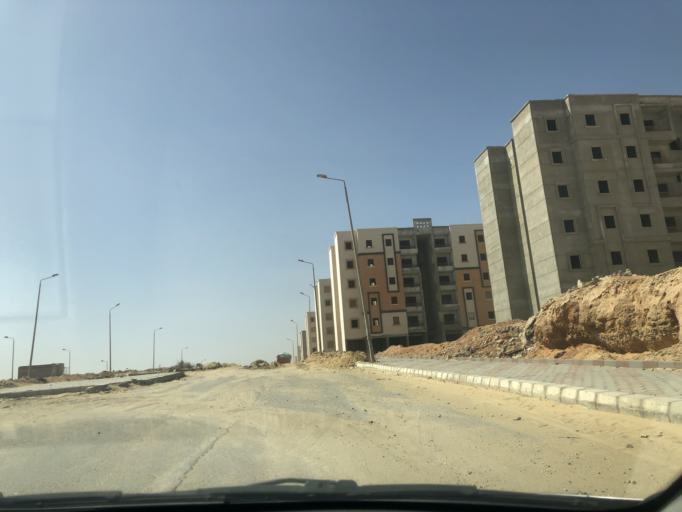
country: EG
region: Al Jizah
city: Madinat Sittah Uktubar
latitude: 29.9339
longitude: 31.0081
